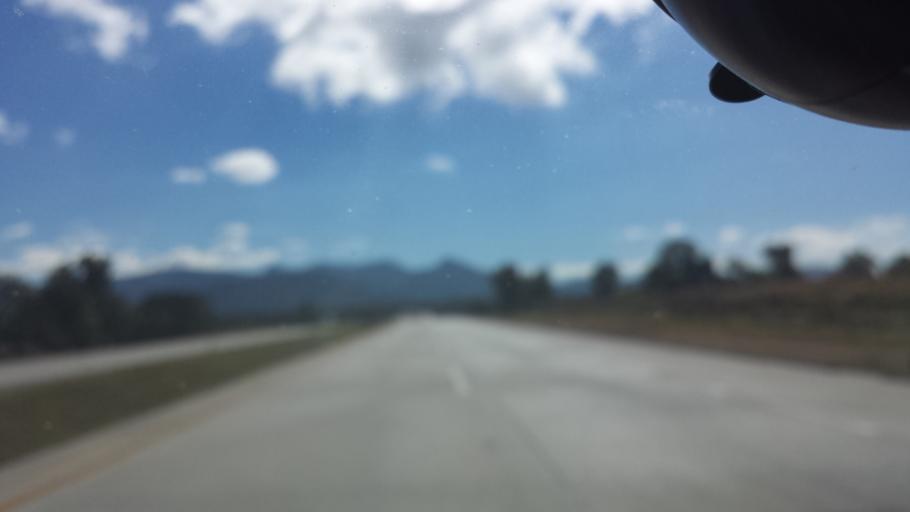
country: MX
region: Hidalgo
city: Doxey
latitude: 20.0752
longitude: -99.2367
